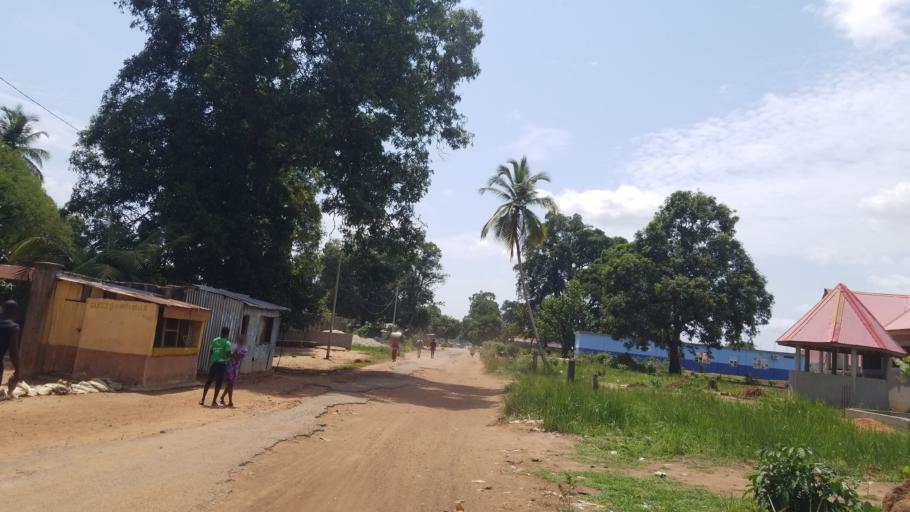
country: SL
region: Western Area
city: Waterloo
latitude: 8.3102
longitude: -13.0531
